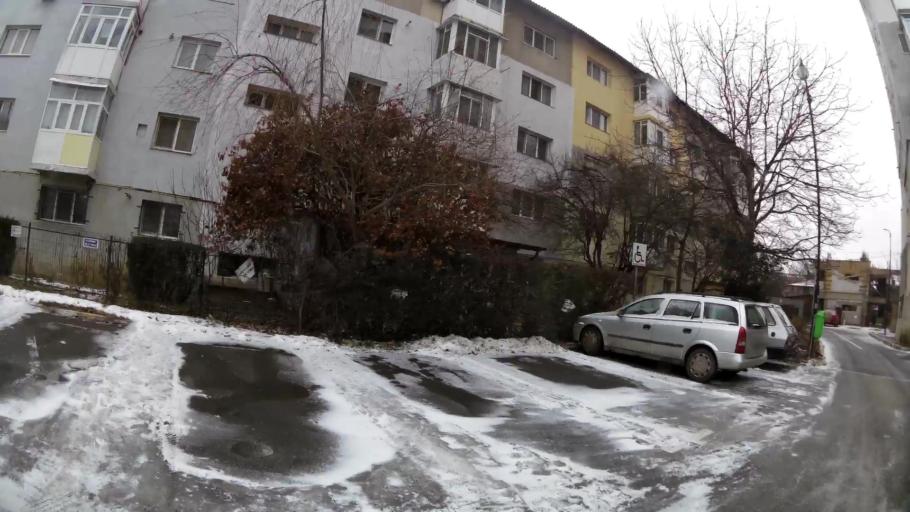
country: RO
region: Dambovita
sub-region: Municipiul Targoviste
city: Targoviste
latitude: 44.9319
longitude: 25.4509
